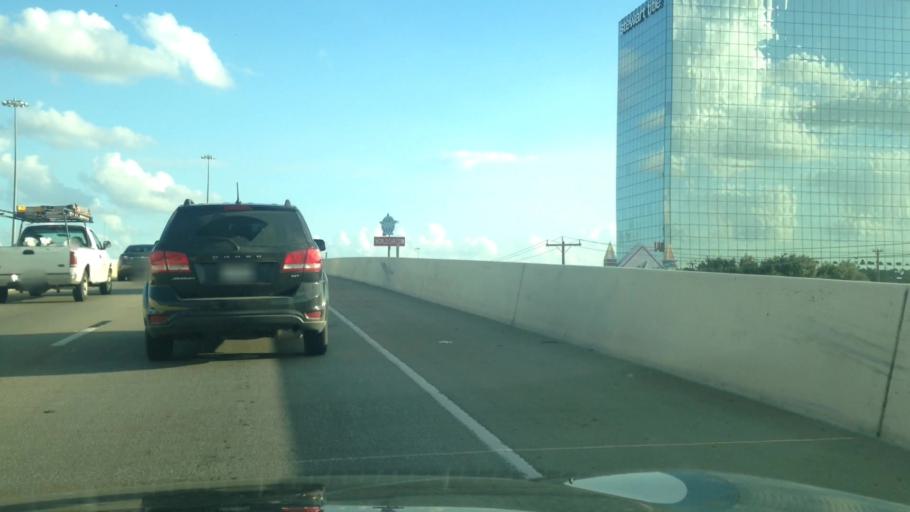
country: US
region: Texas
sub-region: Bexar County
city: Balcones Heights
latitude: 29.5056
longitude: -98.5510
